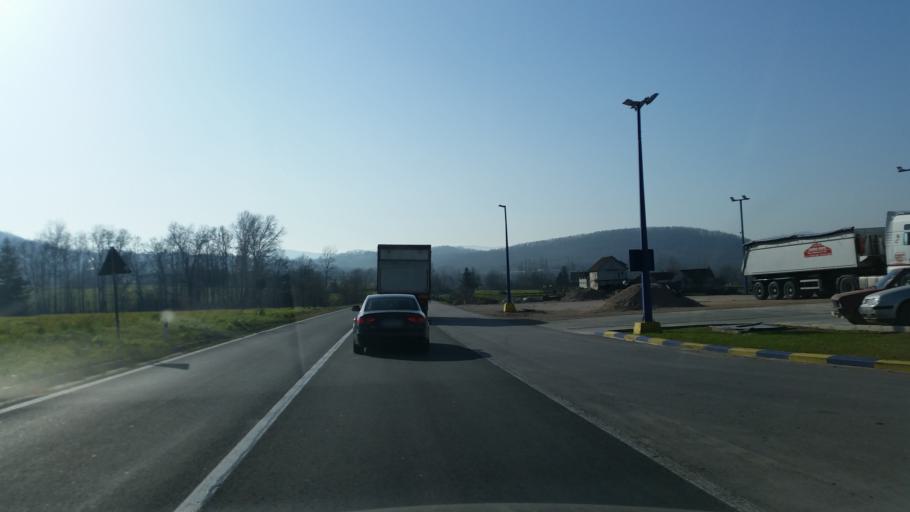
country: RS
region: Central Serbia
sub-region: Kolubarski Okrug
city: Ljig
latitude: 44.2493
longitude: 20.2844
